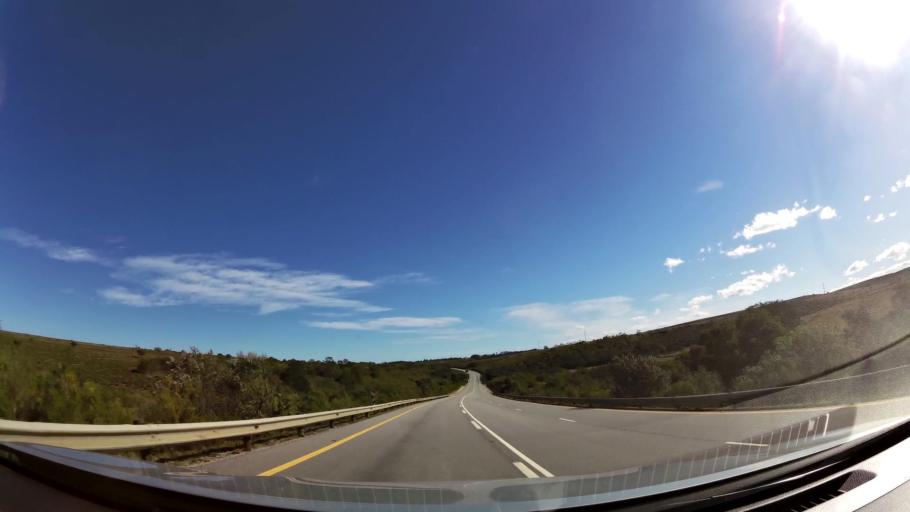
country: ZA
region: Eastern Cape
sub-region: Cacadu District Municipality
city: Kruisfontein
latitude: -34.0138
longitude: 24.6402
